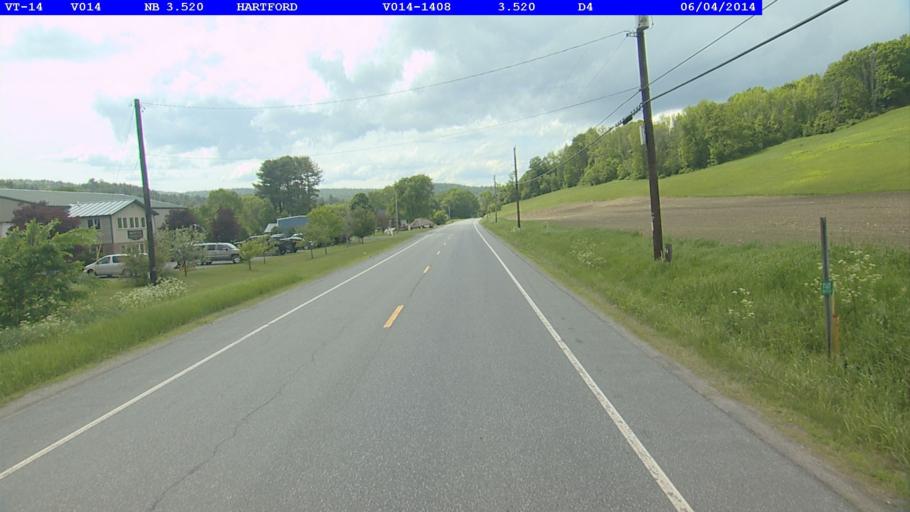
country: US
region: Vermont
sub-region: Windsor County
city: White River Junction
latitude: 43.6736
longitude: -72.3813
